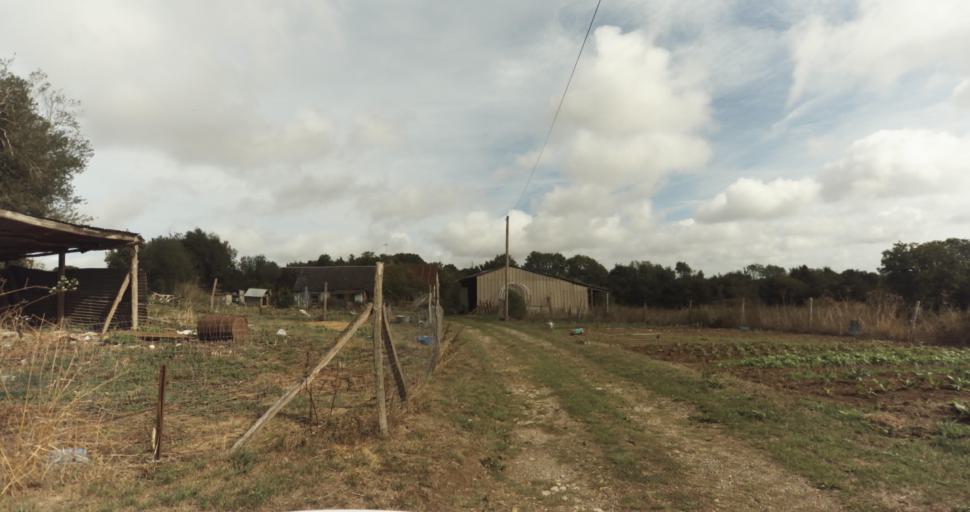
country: FR
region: Lower Normandy
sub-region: Departement de l'Orne
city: Gace
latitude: 48.8448
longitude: 0.3849
